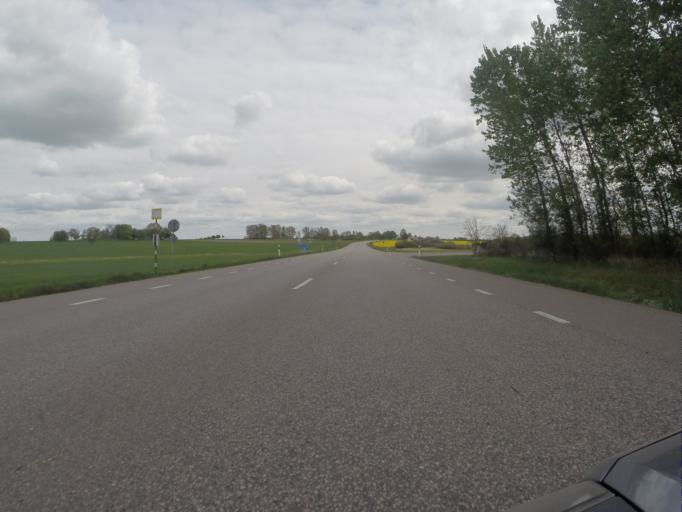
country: SE
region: Skane
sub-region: Helsingborg
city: Hyllinge
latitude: 56.0986
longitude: 12.8005
